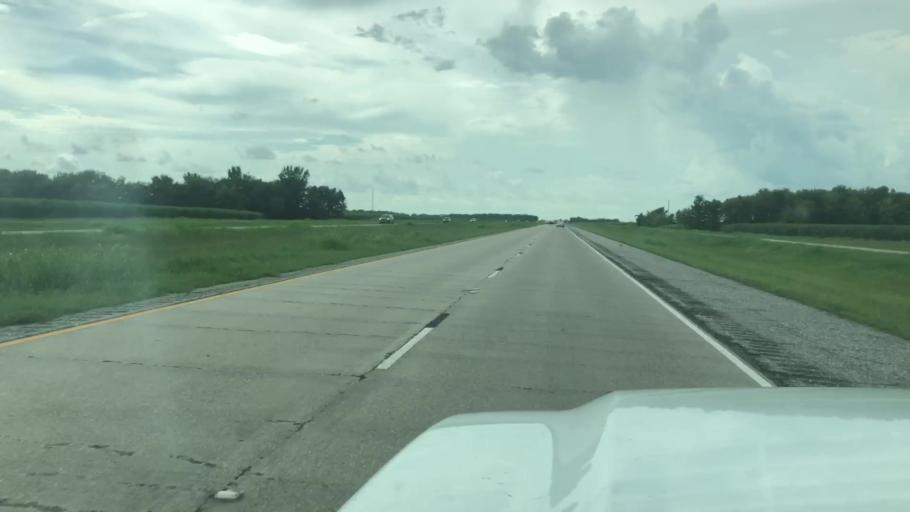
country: US
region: Louisiana
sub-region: Saint Mary Parish
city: Baldwin
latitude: 29.8459
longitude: -91.5865
